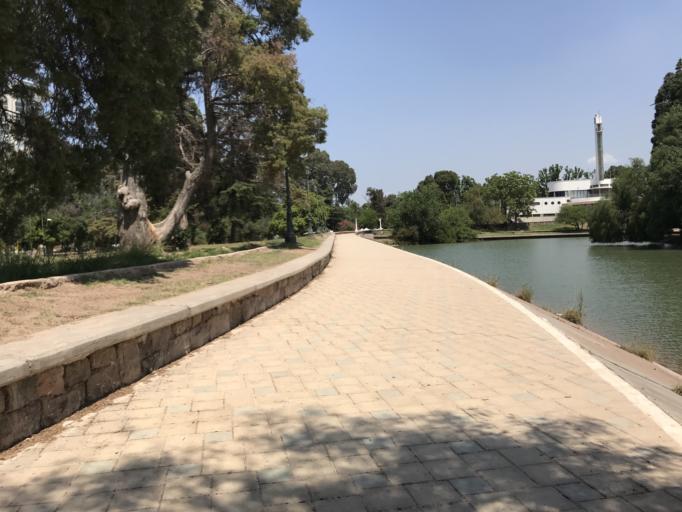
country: AR
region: Mendoza
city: Mendoza
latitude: -32.8966
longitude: -68.8644
